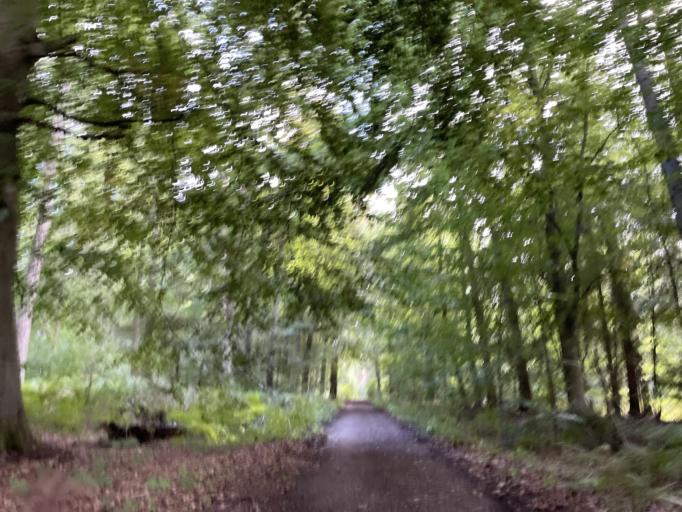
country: DE
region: Lower Saxony
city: Deutsch Evern
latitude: 53.2237
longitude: 10.4266
